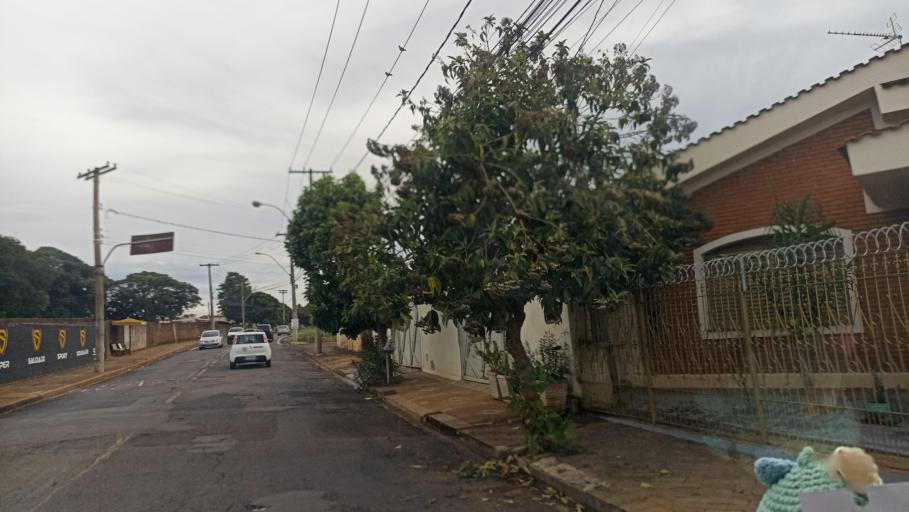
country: BR
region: Sao Paulo
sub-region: Jaboticabal
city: Jaboticabal
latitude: -21.2582
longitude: -48.3285
